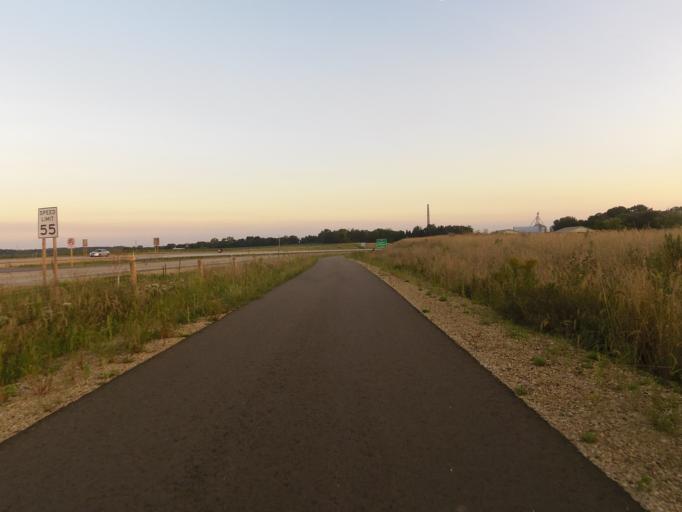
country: US
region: Minnesota
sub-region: Washington County
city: Oak Park Heights
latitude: 45.0524
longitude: -92.7795
